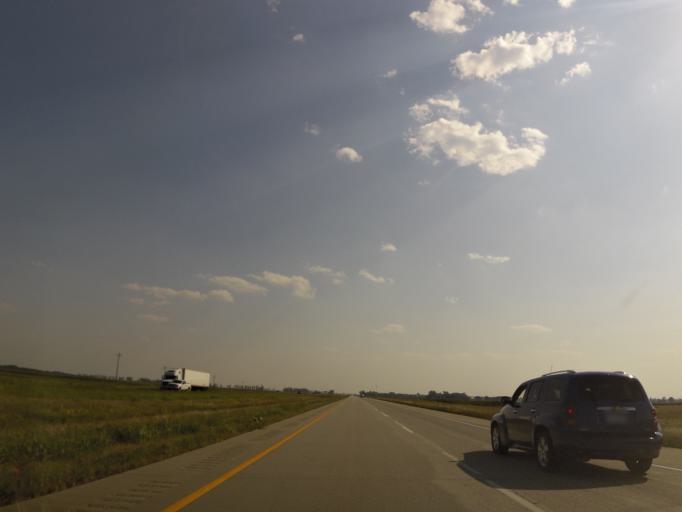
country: US
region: North Dakota
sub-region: Walsh County
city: Grafton
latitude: 48.2248
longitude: -97.1896
